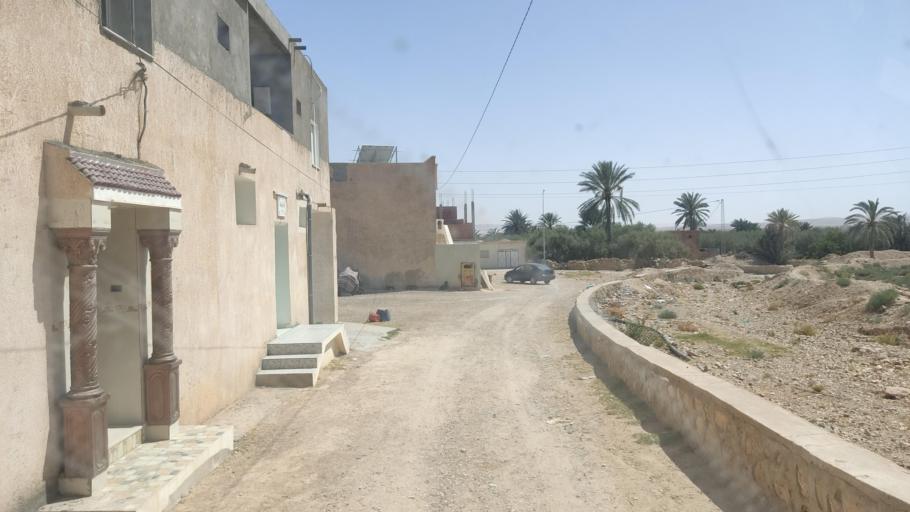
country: TN
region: Gafsa
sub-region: Gafsa Municipality
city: Gafsa
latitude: 34.3377
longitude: 8.9199
